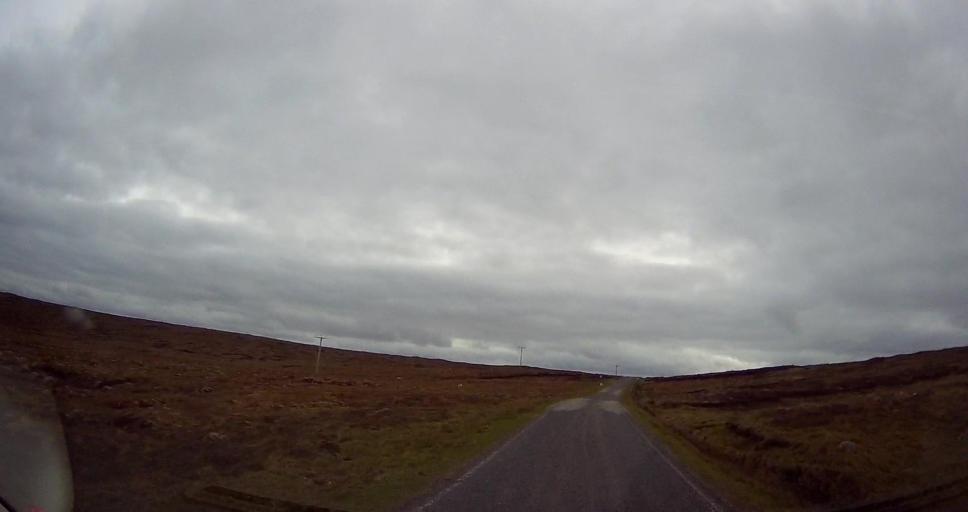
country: GB
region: Scotland
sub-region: Shetland Islands
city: Shetland
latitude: 60.5100
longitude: -1.1287
